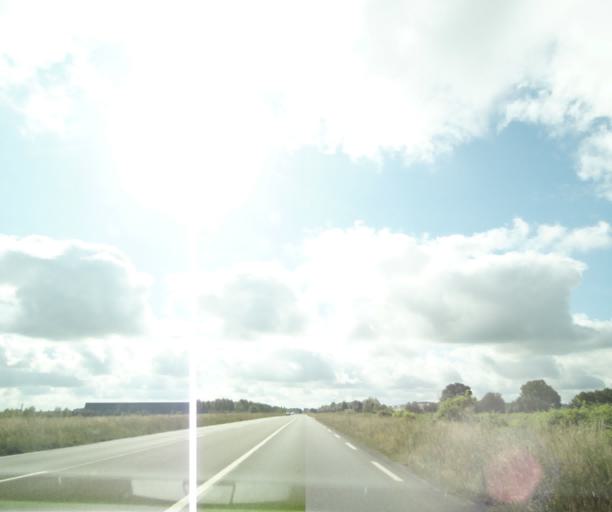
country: FR
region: Pays de la Loire
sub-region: Departement de la Sarthe
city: Vion
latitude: 47.7810
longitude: -0.2267
